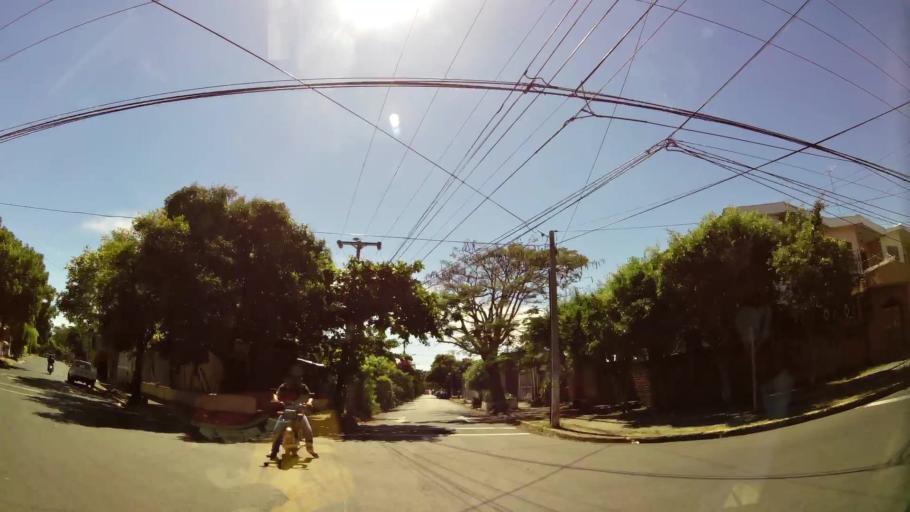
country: SV
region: San Miguel
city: San Miguel
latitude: 13.4784
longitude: -88.1706
